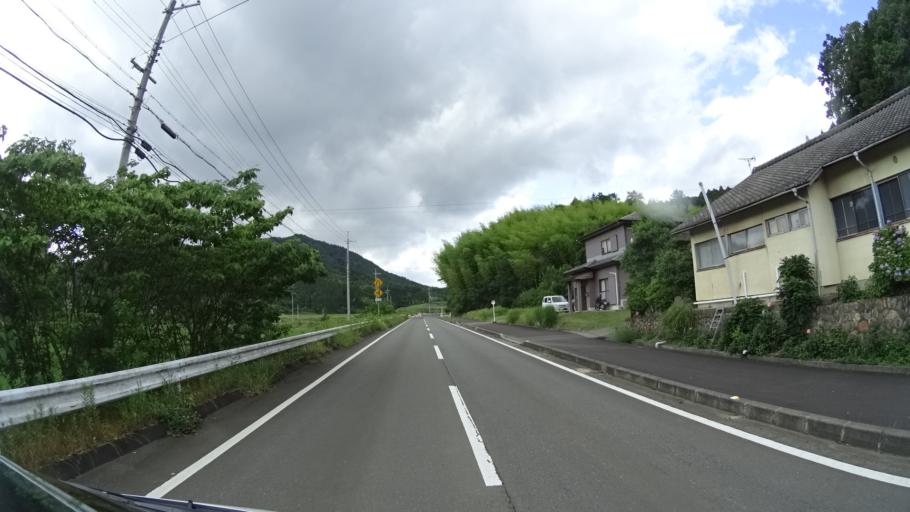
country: JP
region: Kyoto
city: Ayabe
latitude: 35.3325
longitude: 135.2059
